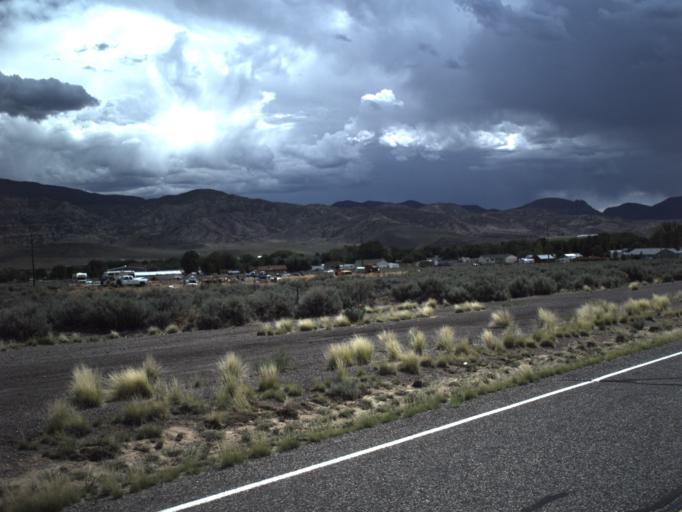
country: US
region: Utah
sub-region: Piute County
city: Junction
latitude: 38.2424
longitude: -112.2312
